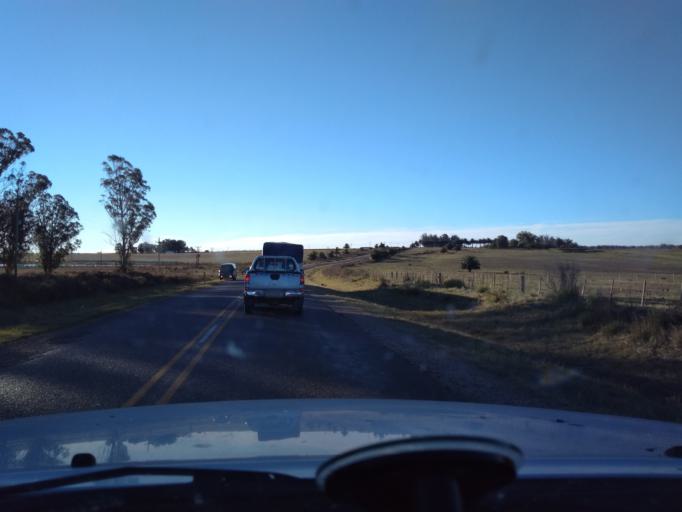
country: UY
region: Canelones
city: San Ramon
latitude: -34.1640
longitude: -55.9467
